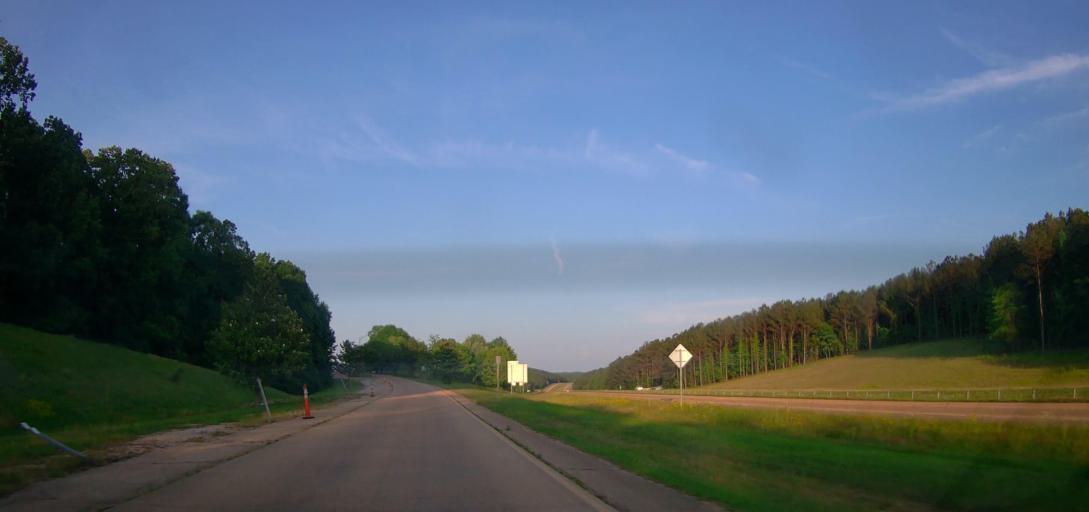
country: US
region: Mississippi
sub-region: Itawamba County
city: Fulton
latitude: 34.2208
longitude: -88.2363
